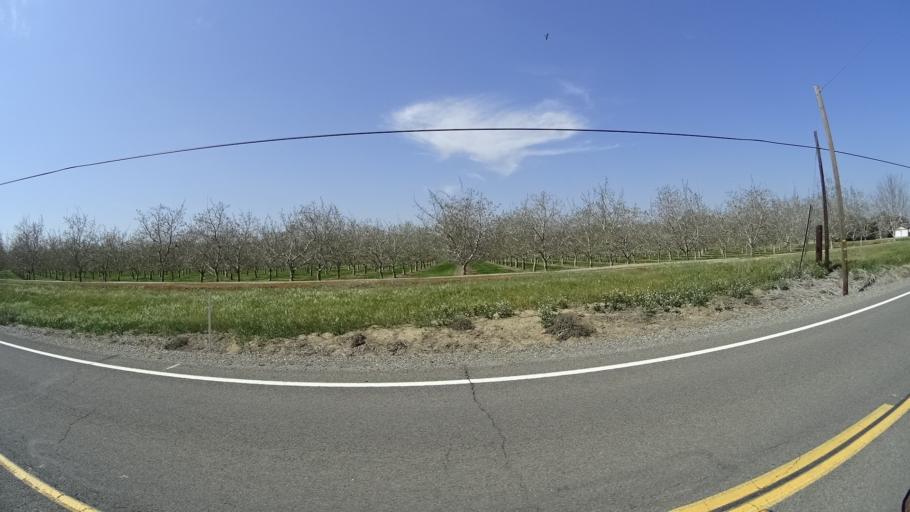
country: US
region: California
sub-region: Glenn County
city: Willows
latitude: 39.4680
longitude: -122.0195
